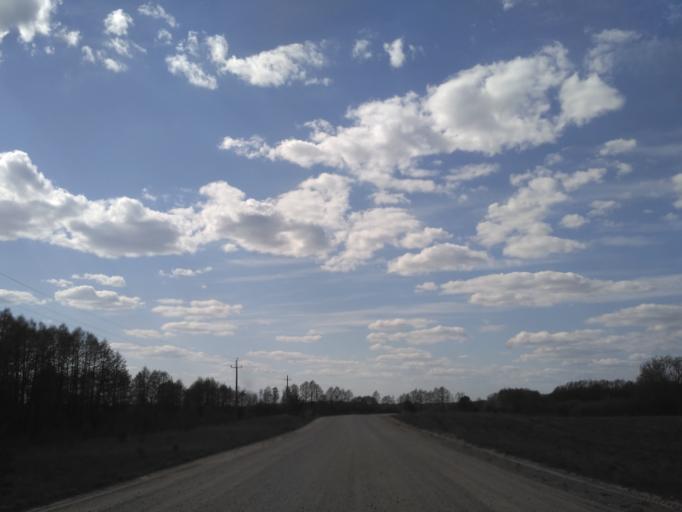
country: BY
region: Minsk
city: Narach
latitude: 54.9940
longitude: 26.5638
